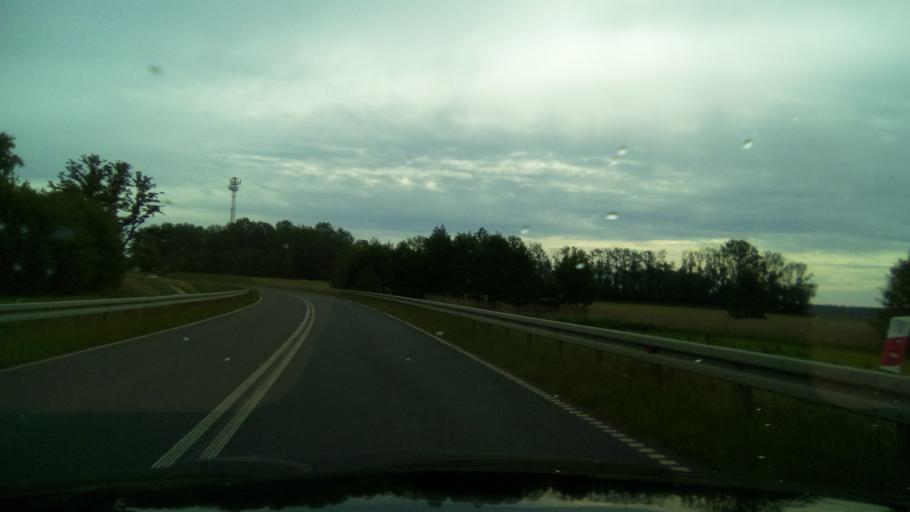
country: PL
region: Kujawsko-Pomorskie
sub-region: Powiat nakielski
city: Mrocza
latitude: 53.2330
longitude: 17.6106
